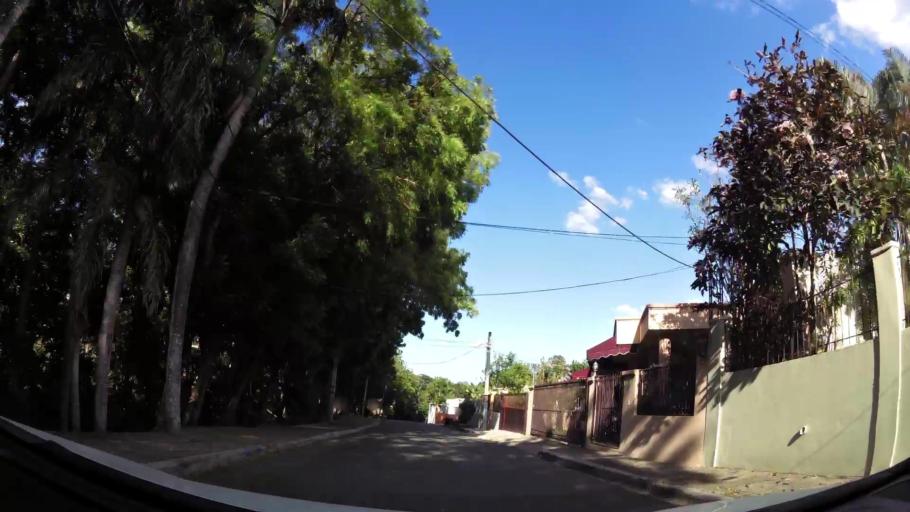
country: DO
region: Nacional
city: Santo Domingo
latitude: 18.5120
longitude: -69.9774
